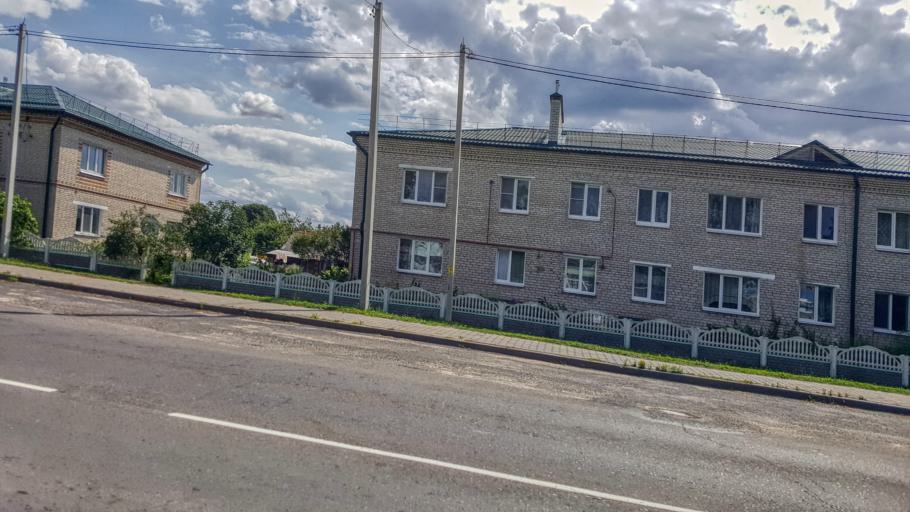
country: BY
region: Brest
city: Kamyanyets
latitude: 52.3954
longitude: 23.8303
